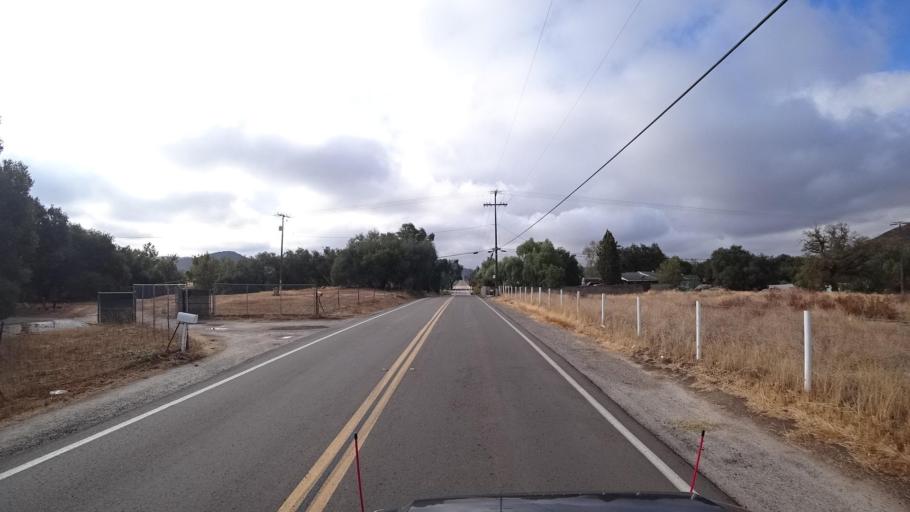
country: MX
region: Baja California
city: Tecate
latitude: 32.6228
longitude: -116.6135
